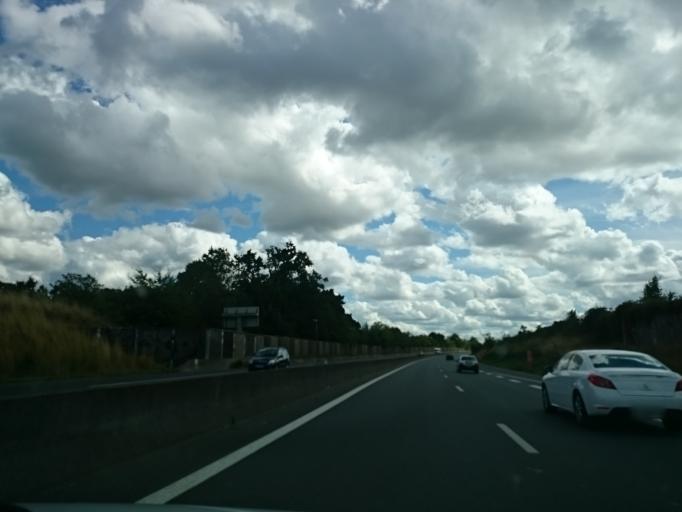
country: FR
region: Pays de la Loire
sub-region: Departement de la Loire-Atlantique
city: Sainte-Luce-sur-Loire
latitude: 47.2506
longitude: -1.4765
